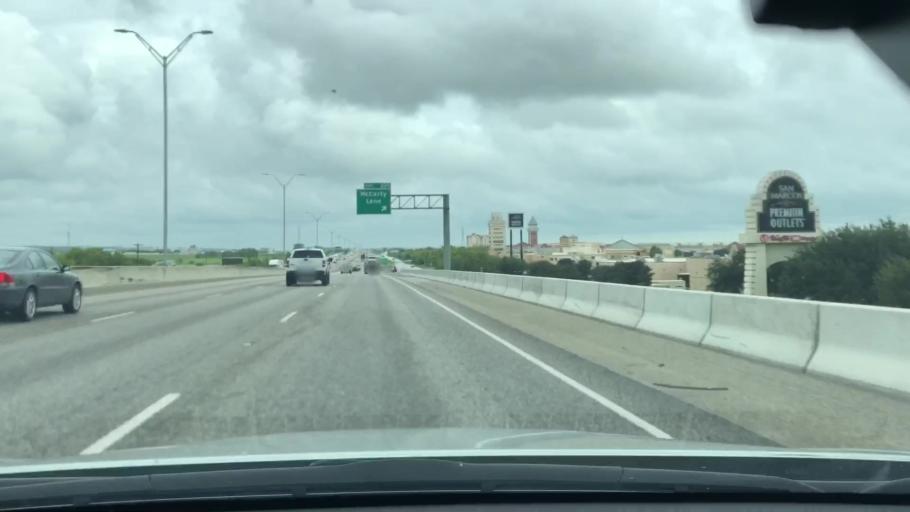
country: US
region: Texas
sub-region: Hays County
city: San Marcos
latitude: 29.8275
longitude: -97.9895
